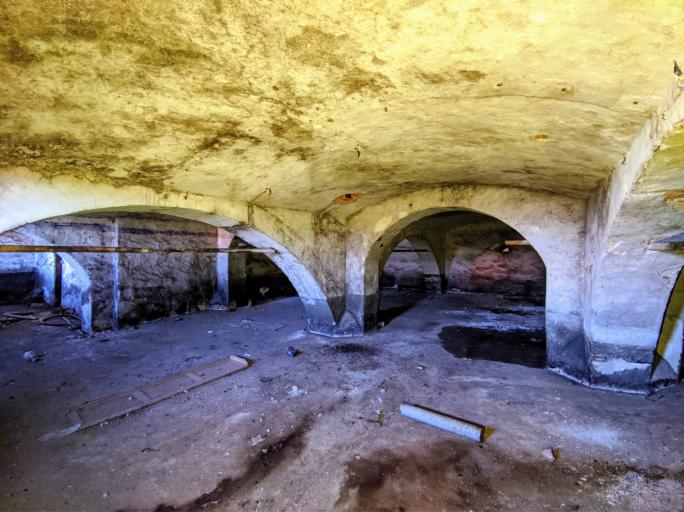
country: PL
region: Lubusz
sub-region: Powiat sulecinski
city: Lubniewice
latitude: 52.4744
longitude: 15.2382
